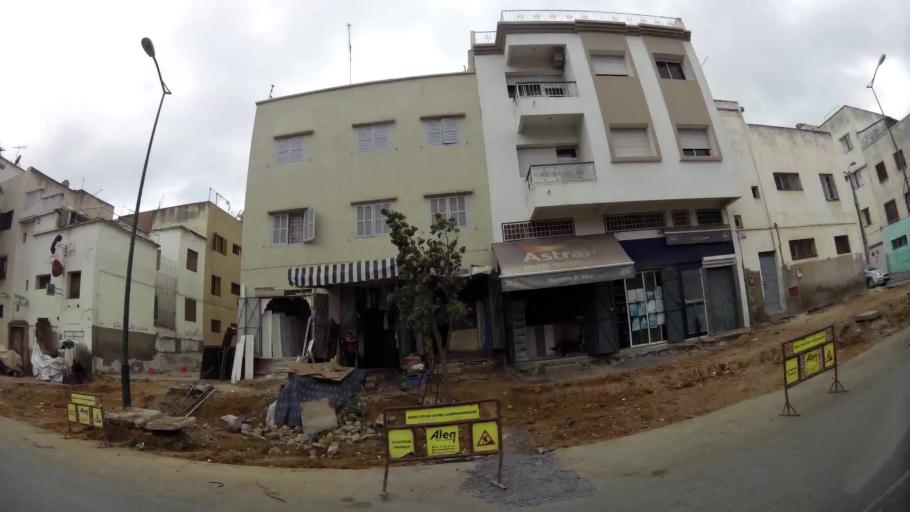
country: MA
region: Rabat-Sale-Zemmour-Zaer
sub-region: Rabat
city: Rabat
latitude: 33.9942
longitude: -6.8158
